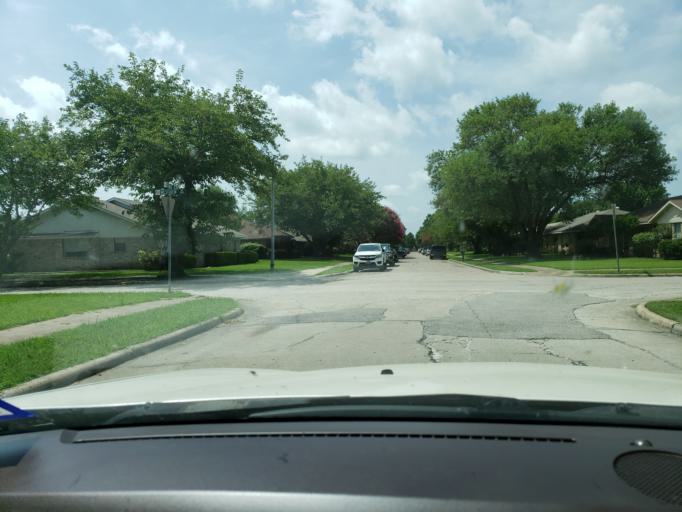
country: US
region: Texas
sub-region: Dallas County
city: Rowlett
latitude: 32.8977
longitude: -96.5619
